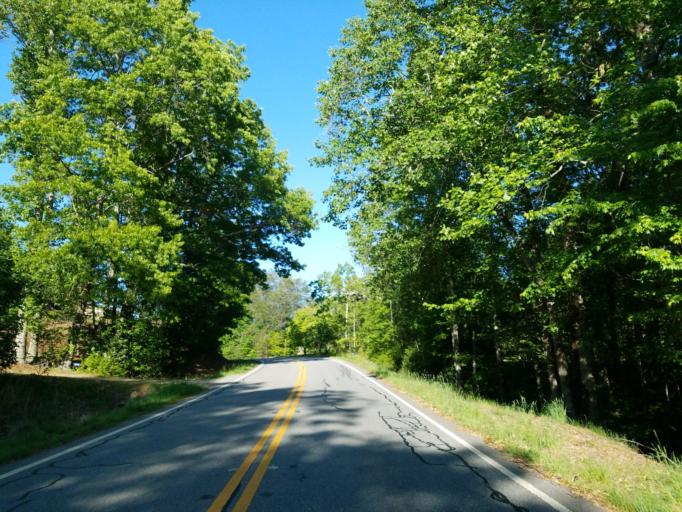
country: US
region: Georgia
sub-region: Fannin County
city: Blue Ridge
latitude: 34.8432
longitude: -84.2066
